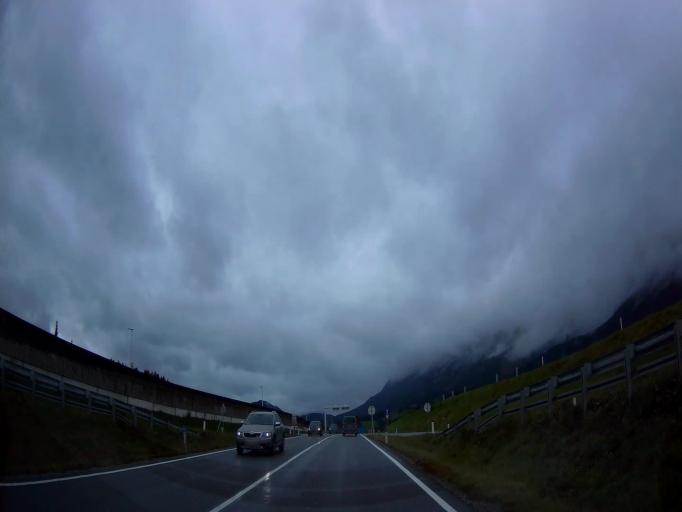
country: AT
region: Tyrol
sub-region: Politischer Bezirk Kufstein
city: Ellmau
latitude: 47.5164
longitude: 12.2952
